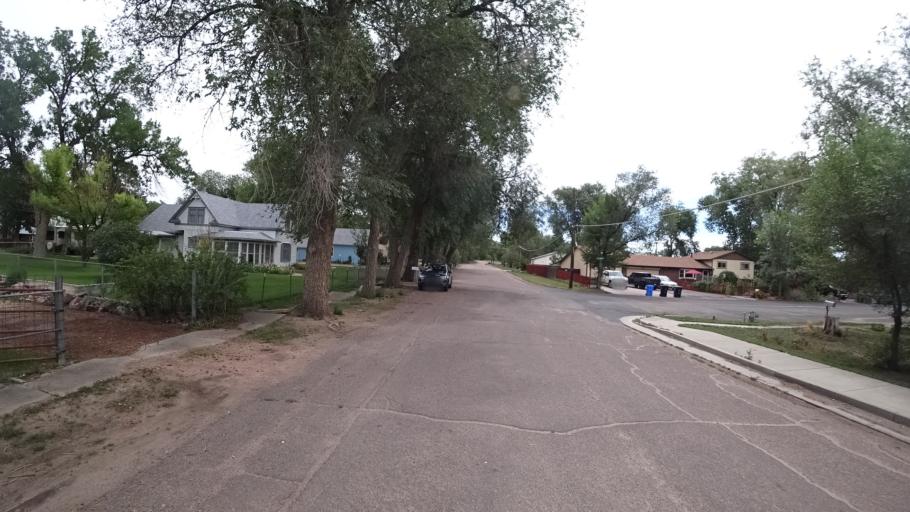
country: US
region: Colorado
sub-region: El Paso County
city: Fountain
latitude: 38.6870
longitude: -104.7010
